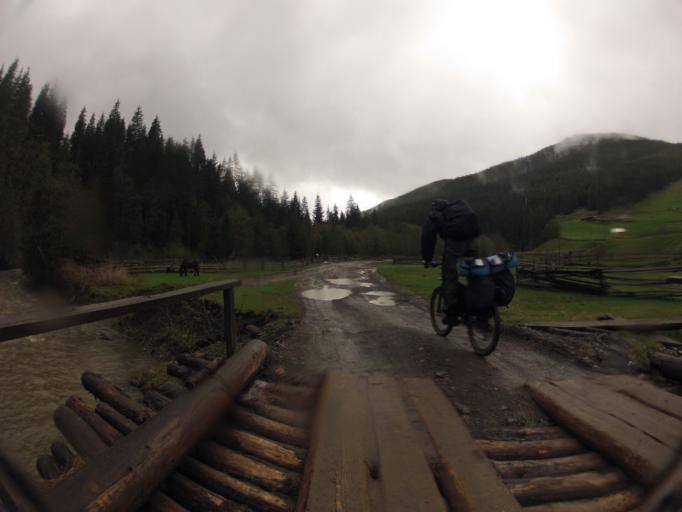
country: RO
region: Suceava
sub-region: Comuna Izvoarele Sucevei
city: Izvoarele Sucevei
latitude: 47.8323
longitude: 25.0500
